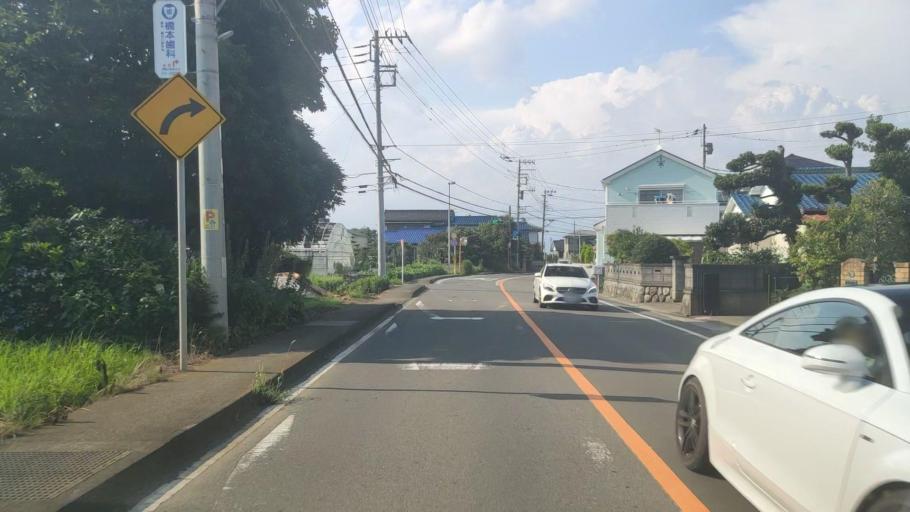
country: JP
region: Kanagawa
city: Isehara
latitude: 35.3707
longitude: 139.3283
